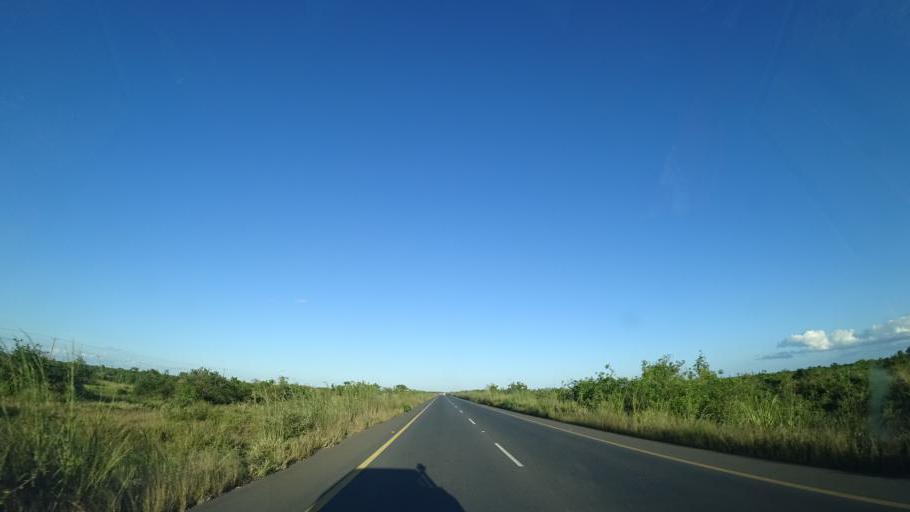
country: MZ
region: Sofala
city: Dondo
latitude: -19.3229
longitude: 34.2982
